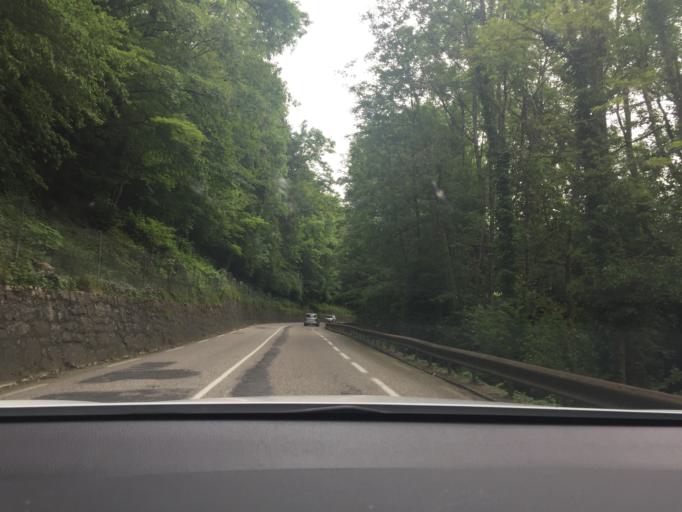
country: FR
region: Rhone-Alpes
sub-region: Departement de la Savoie
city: Vimines
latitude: 45.5309
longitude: 5.8621
